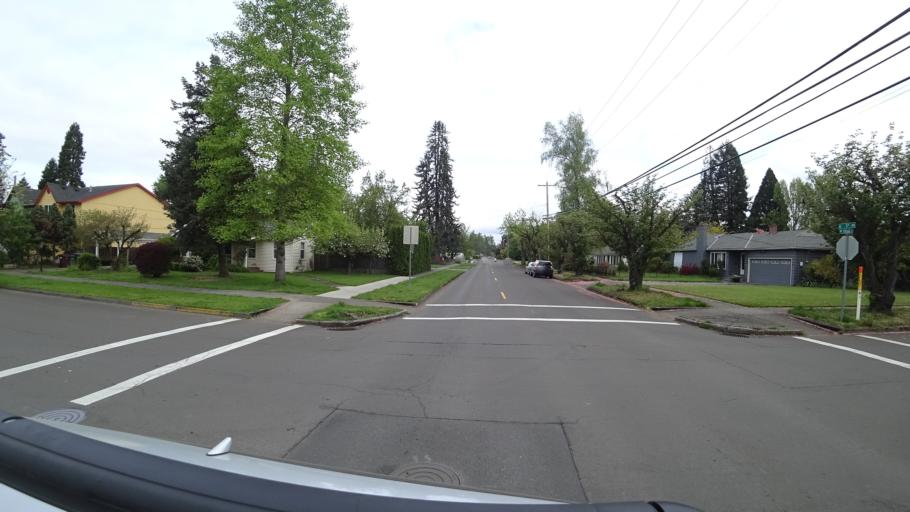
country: US
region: Oregon
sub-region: Washington County
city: Hillsboro
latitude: 45.5262
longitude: -122.9825
